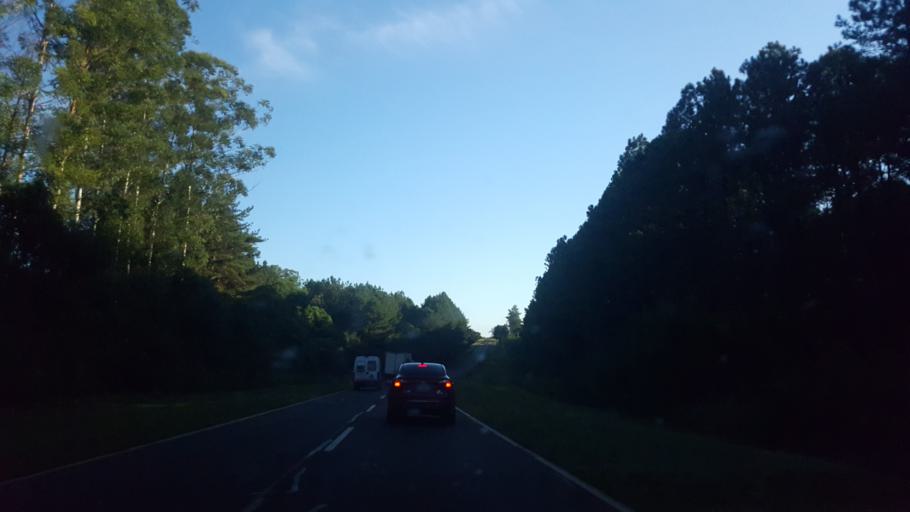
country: AR
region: Misiones
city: El Alcazar
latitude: -26.7379
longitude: -54.8769
